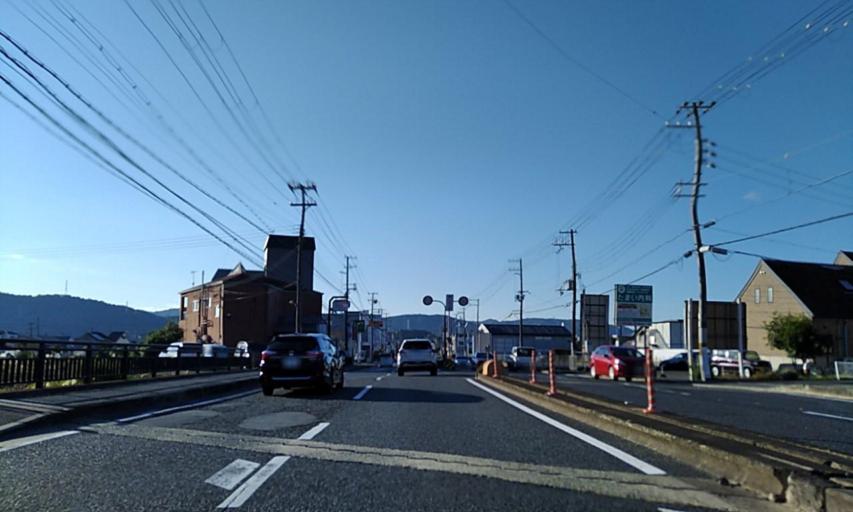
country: JP
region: Wakayama
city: Kainan
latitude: 34.1800
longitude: 135.1862
